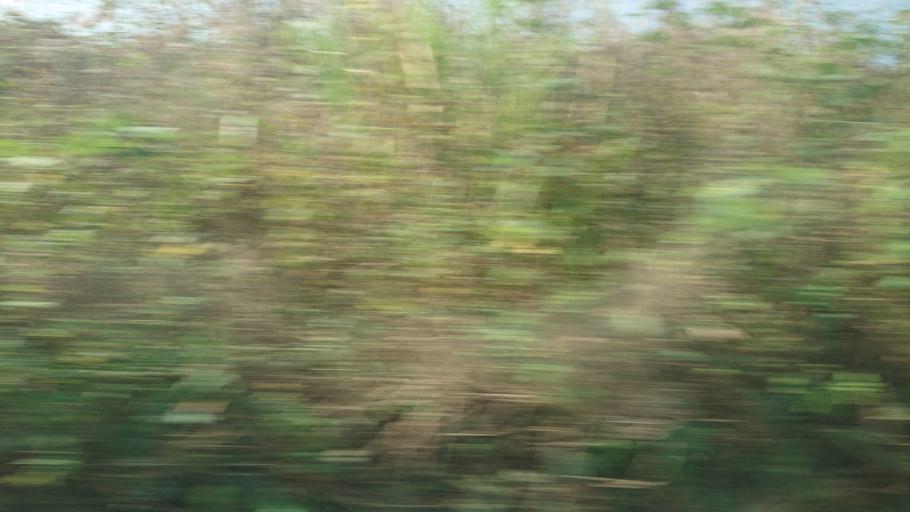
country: TW
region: Taiwan
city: Lugu
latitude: 23.7335
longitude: 120.6596
